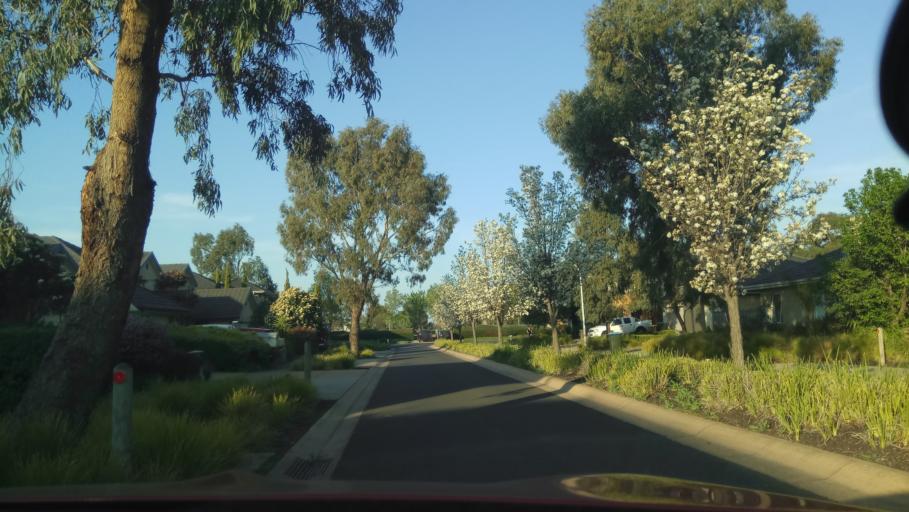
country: AU
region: Victoria
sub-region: Hobsons Bay
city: Altona Meadows
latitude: -37.8910
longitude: 144.7676
